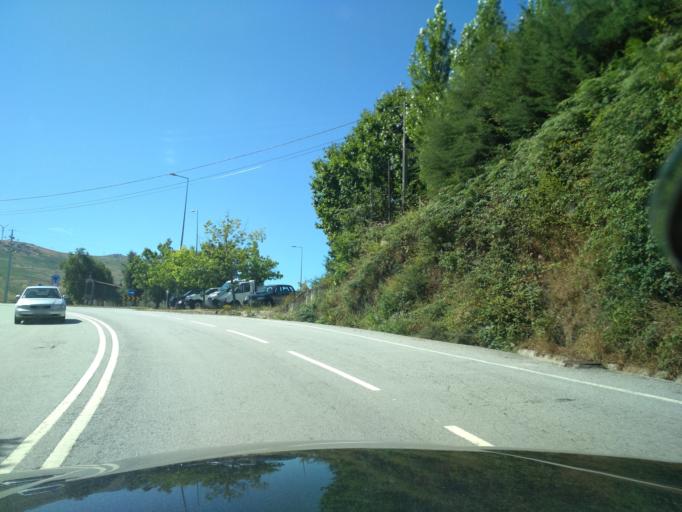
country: PT
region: Vila Real
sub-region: Ribeira de Pena
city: Ribeira de Pena
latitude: 41.5027
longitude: -7.7956
